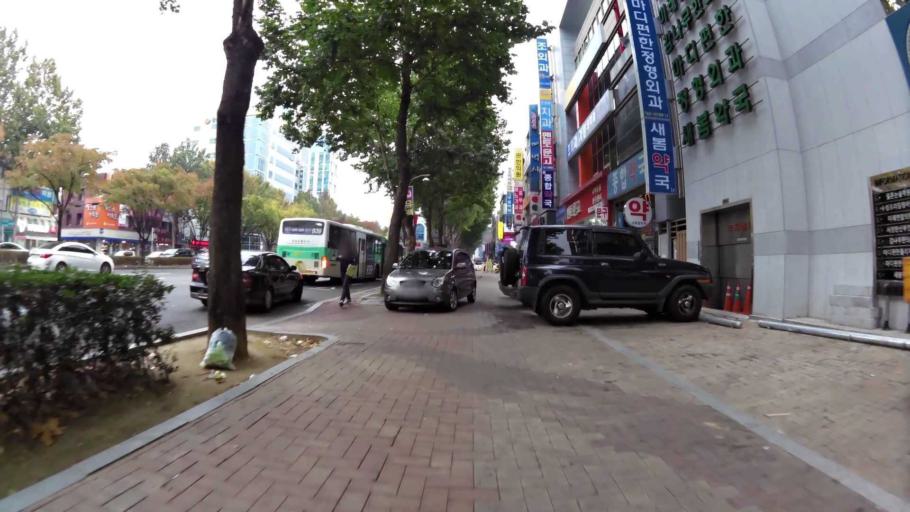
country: KR
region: Daegu
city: Daegu
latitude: 35.8586
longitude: 128.6373
